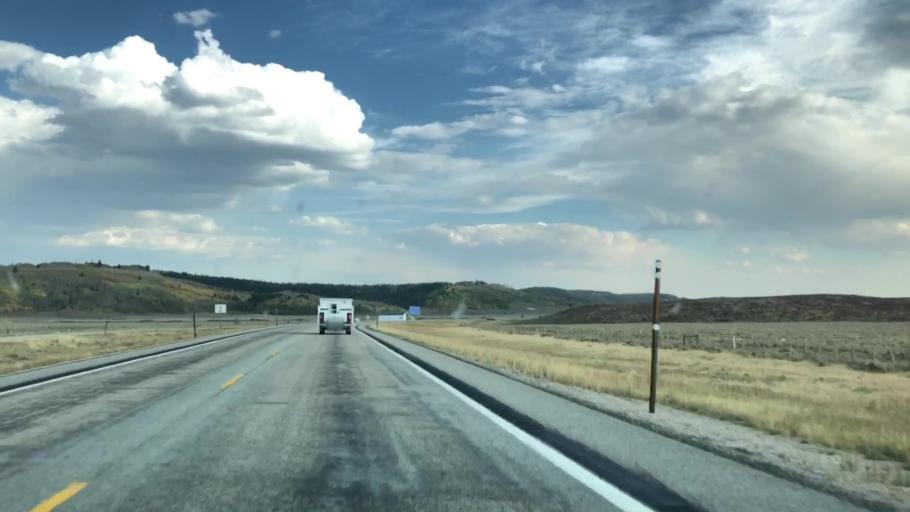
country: US
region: Wyoming
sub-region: Sublette County
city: Pinedale
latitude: 43.1194
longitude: -110.1802
